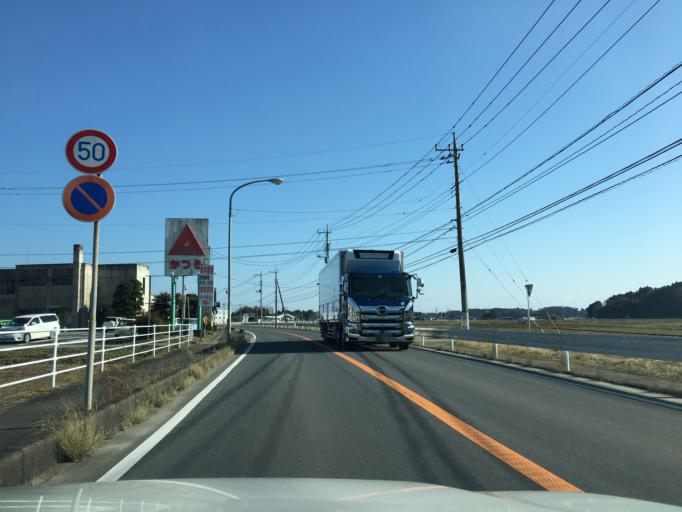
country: JP
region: Ibaraki
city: Omiya
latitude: 36.5125
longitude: 140.3678
